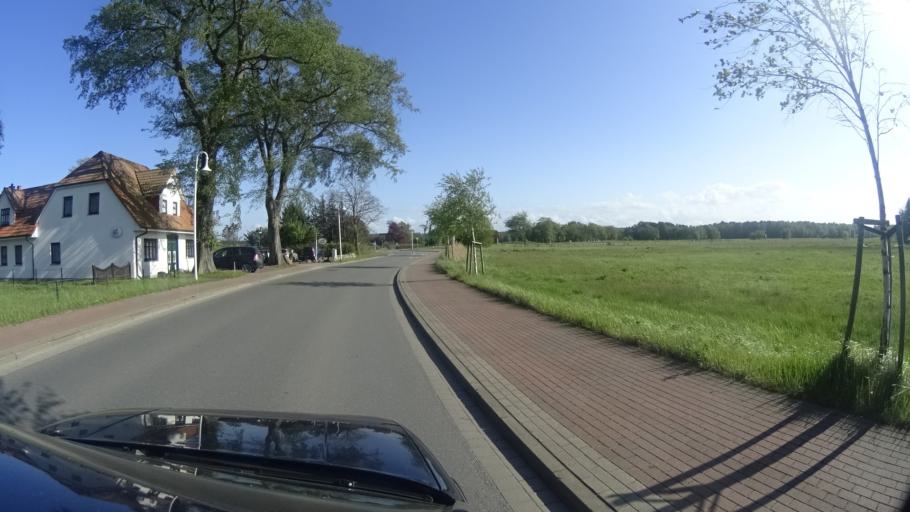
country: DE
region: Mecklenburg-Vorpommern
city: Ostseebad Prerow
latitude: 54.4412
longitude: 12.5792
